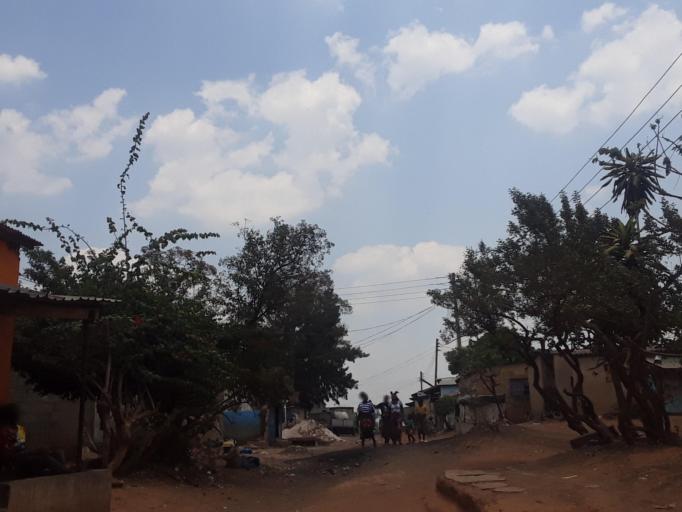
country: ZM
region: Lusaka
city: Lusaka
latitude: -15.3647
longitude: 28.3009
